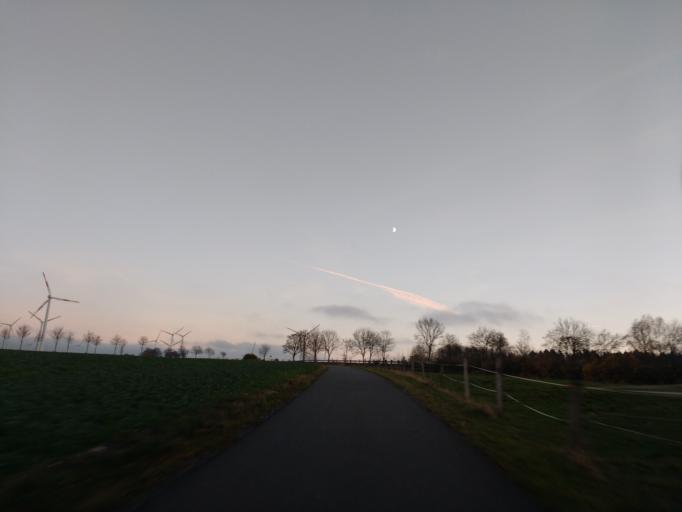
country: DE
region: North Rhine-Westphalia
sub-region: Regierungsbezirk Detmold
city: Paderborn
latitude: 51.6901
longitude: 8.7986
